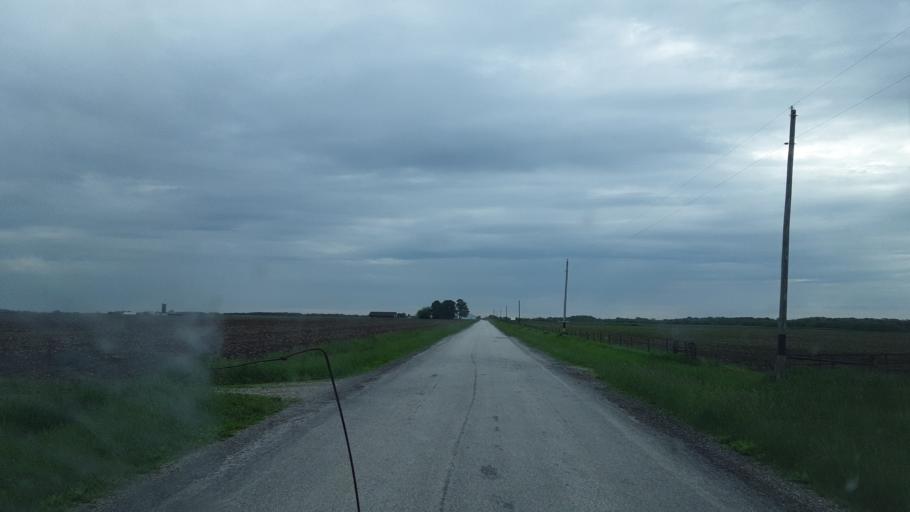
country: US
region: Illinois
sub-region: McDonough County
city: Macomb
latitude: 40.3818
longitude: -90.6388
